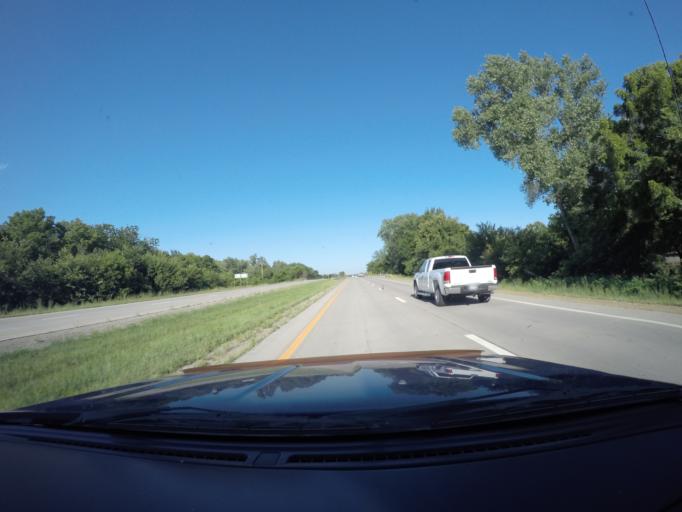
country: US
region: Kansas
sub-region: Shawnee County
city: Topeka
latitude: 39.0874
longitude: -95.5566
